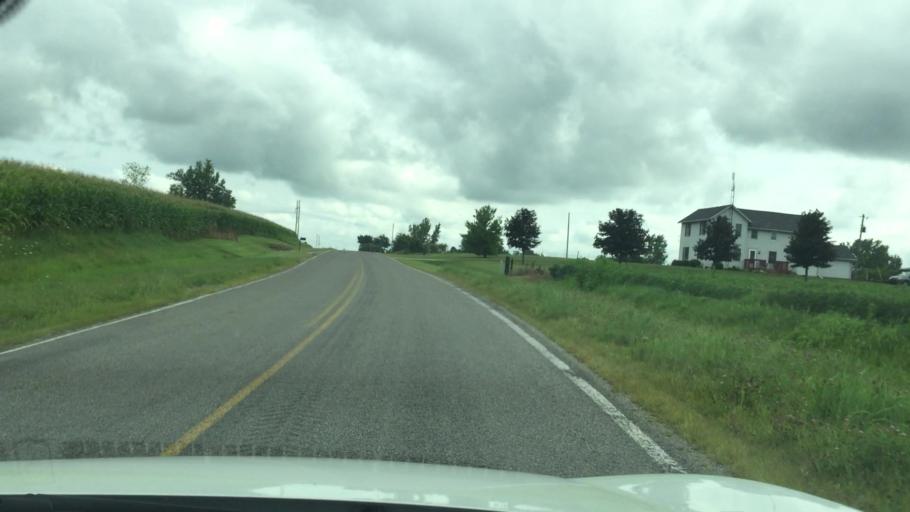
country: US
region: Ohio
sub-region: Champaign County
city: Mechanicsburg
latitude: 40.0592
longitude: -83.6548
